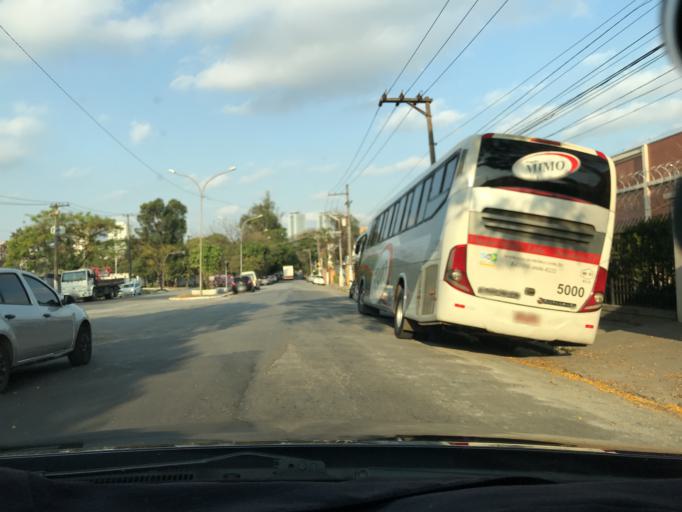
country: BR
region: Sao Paulo
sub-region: Osasco
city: Osasco
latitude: -23.5336
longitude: -46.7524
